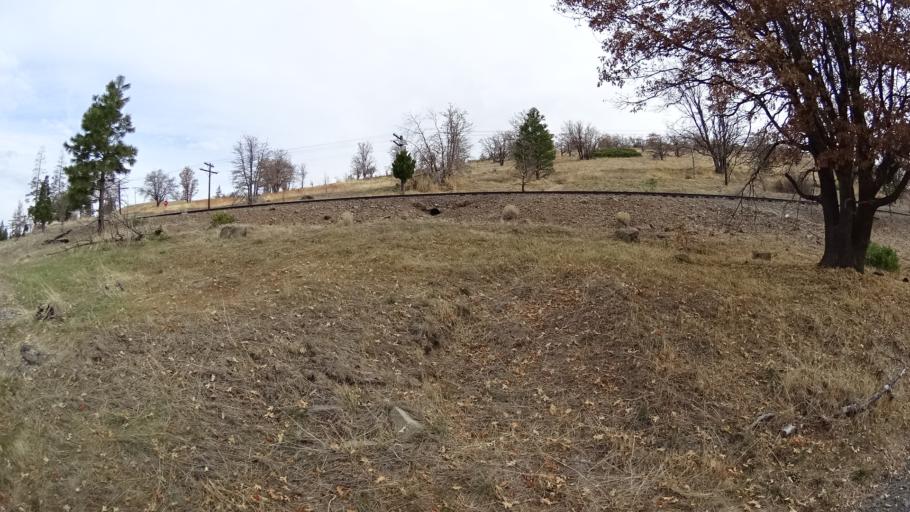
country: US
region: California
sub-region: Siskiyou County
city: Weed
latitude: 41.4243
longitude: -122.3820
